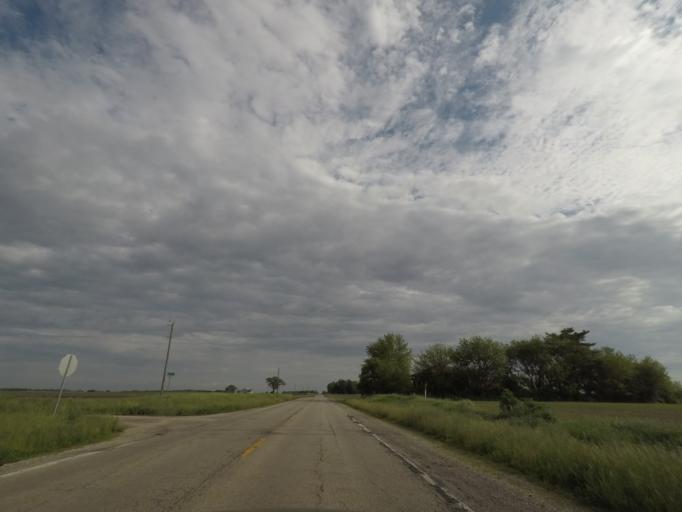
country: US
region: Illinois
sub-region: Logan County
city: Mount Pulaski
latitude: 40.0323
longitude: -89.2821
